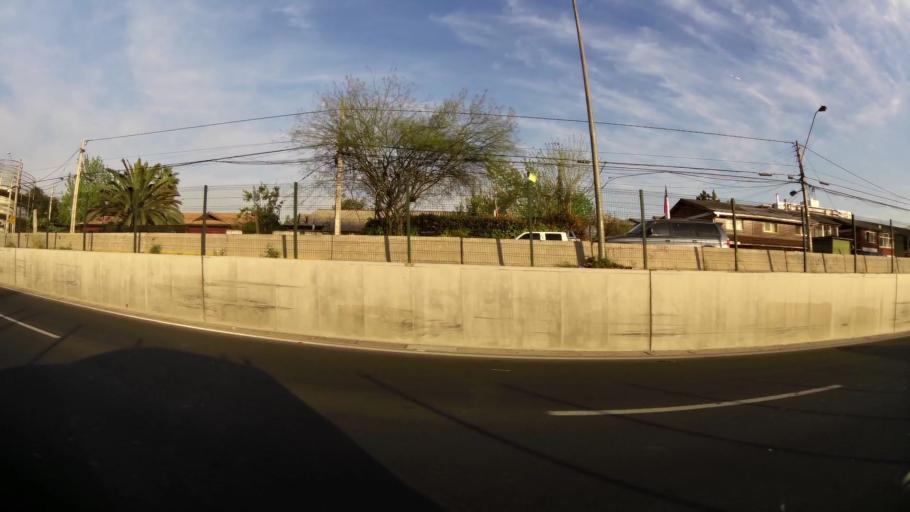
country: CL
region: Santiago Metropolitan
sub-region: Provincia de Santiago
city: Villa Presidente Frei, Nunoa, Santiago, Chile
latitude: -33.4917
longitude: -70.5820
